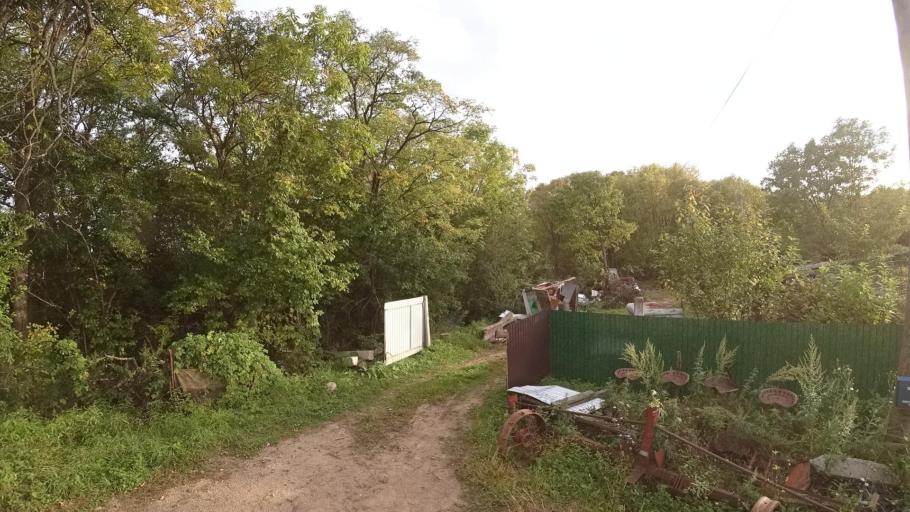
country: RU
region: Primorskiy
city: Yakovlevka
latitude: 44.4172
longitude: 133.4472
